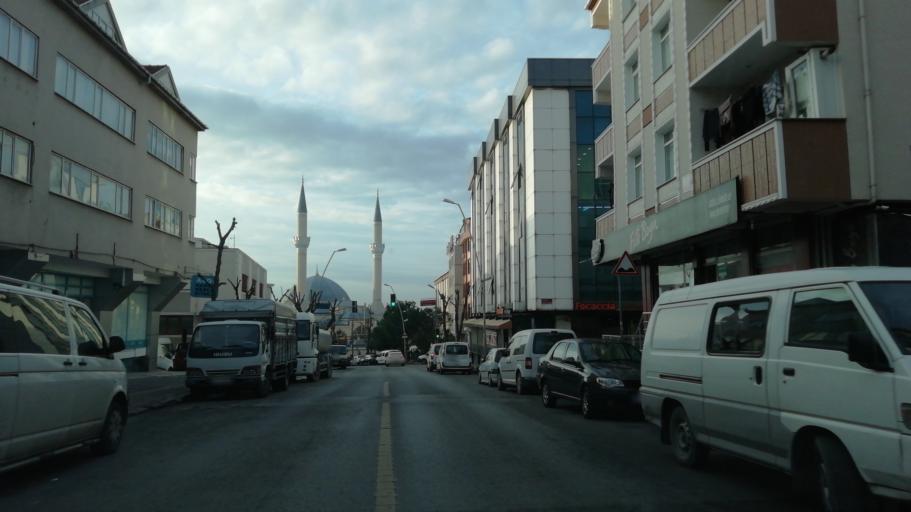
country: TR
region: Istanbul
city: Bahcelievler
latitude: 41.0085
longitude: 28.8276
